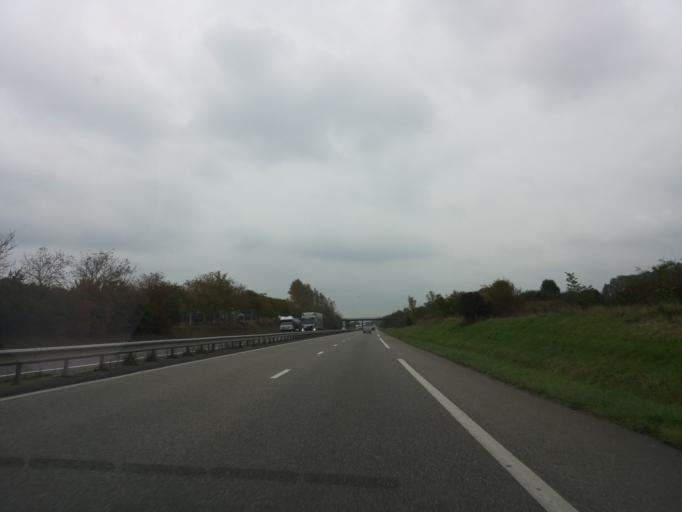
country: FR
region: Lorraine
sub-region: Departement de la Moselle
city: Reding
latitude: 48.7381
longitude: 7.0991
